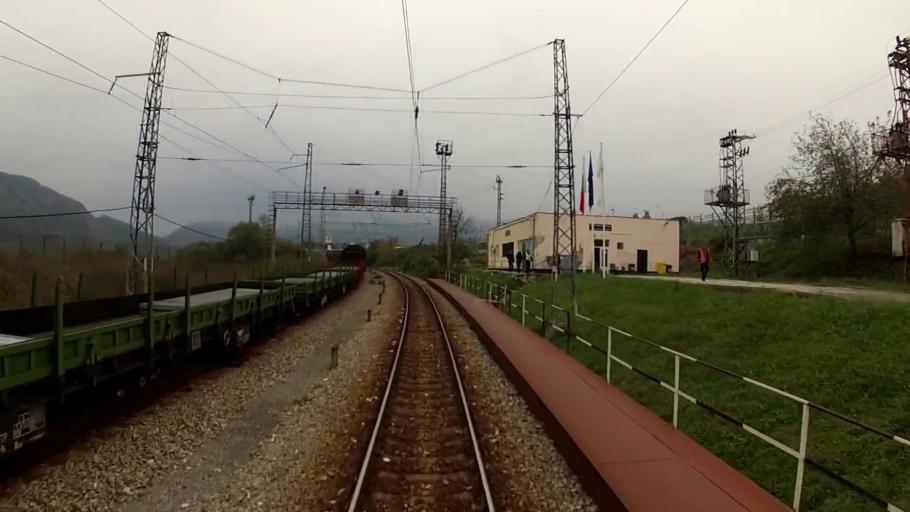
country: RS
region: Central Serbia
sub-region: Pirotski Okrug
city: Dimitrovgrad
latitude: 42.9955
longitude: 22.8406
